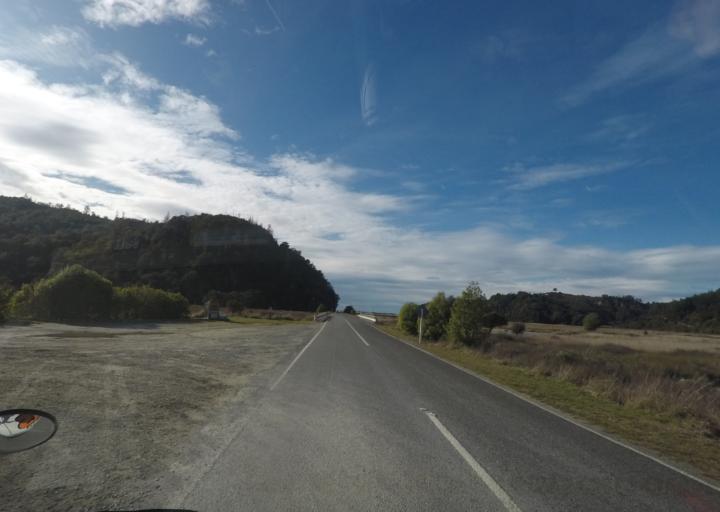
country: NZ
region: Tasman
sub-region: Tasman District
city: Motueka
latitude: -41.0152
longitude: 172.9914
